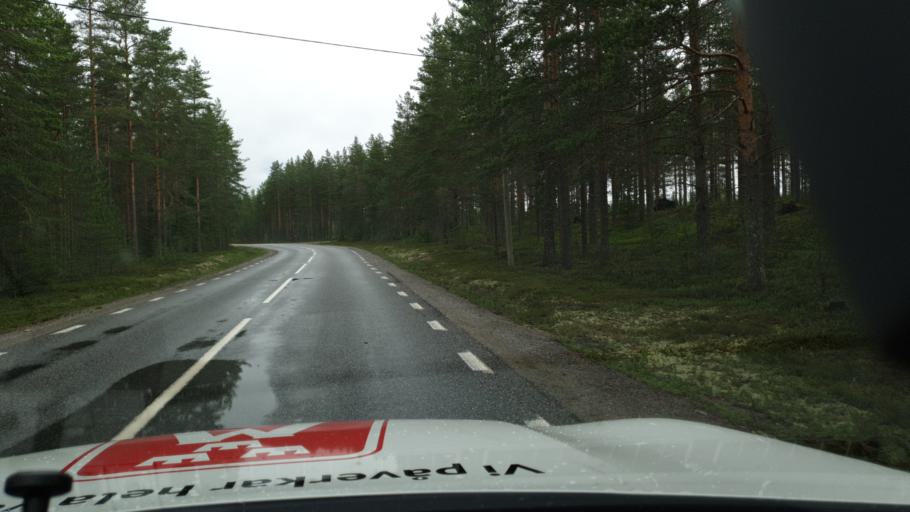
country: SE
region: Vaesterbotten
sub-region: Umea Kommun
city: Saevar
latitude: 63.9958
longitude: 20.4951
